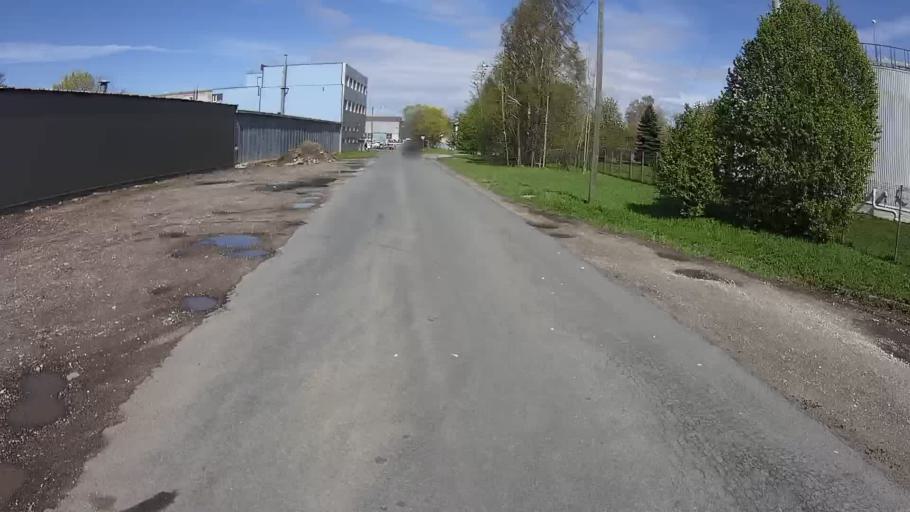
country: EE
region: Harju
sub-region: Tallinna linn
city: Tallinn
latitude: 59.4233
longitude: 24.6915
